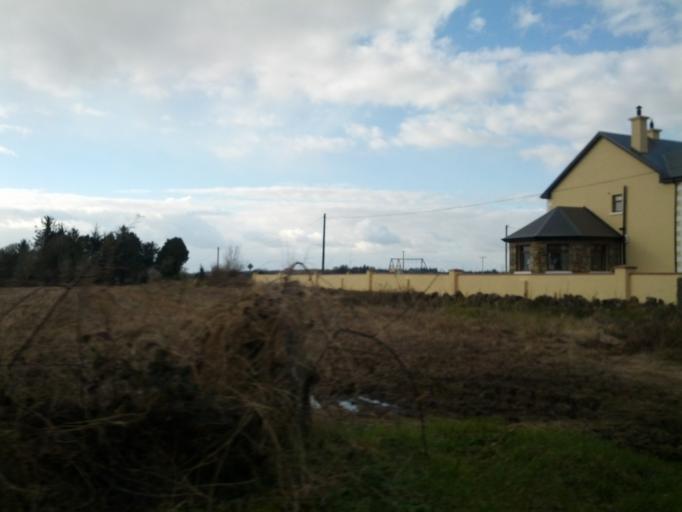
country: IE
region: Connaught
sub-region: County Galway
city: Athenry
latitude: 53.4549
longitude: -8.6431
